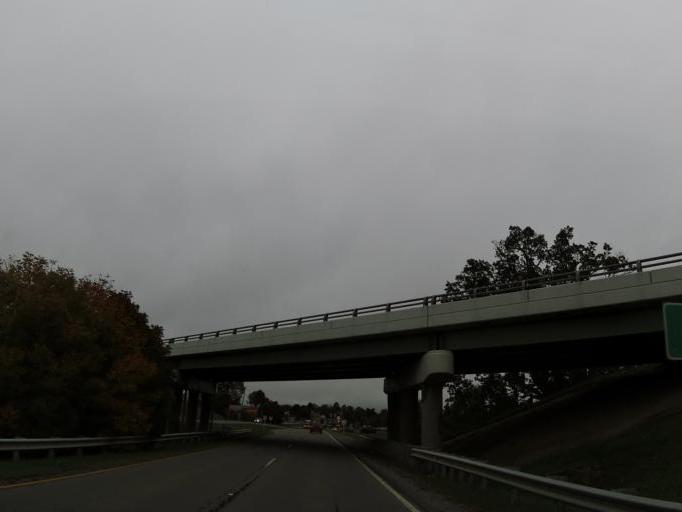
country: US
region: Virginia
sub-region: Wythe County
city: Wytheville
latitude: 36.9601
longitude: -81.0992
